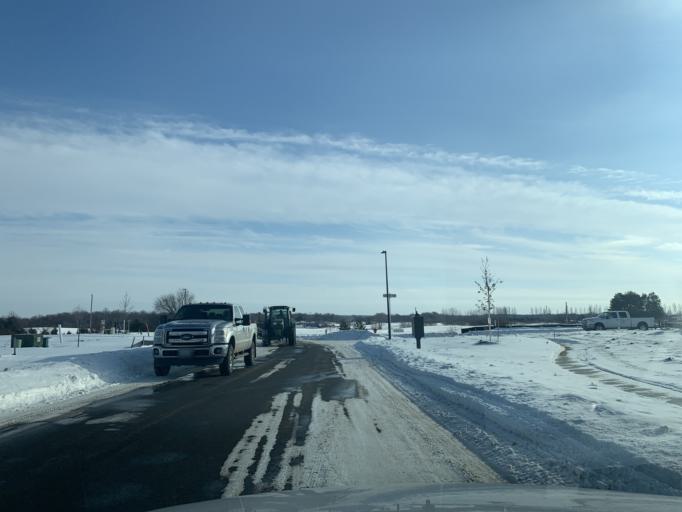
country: US
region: Minnesota
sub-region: Wright County
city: Buffalo
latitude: 45.2048
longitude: -93.8285
